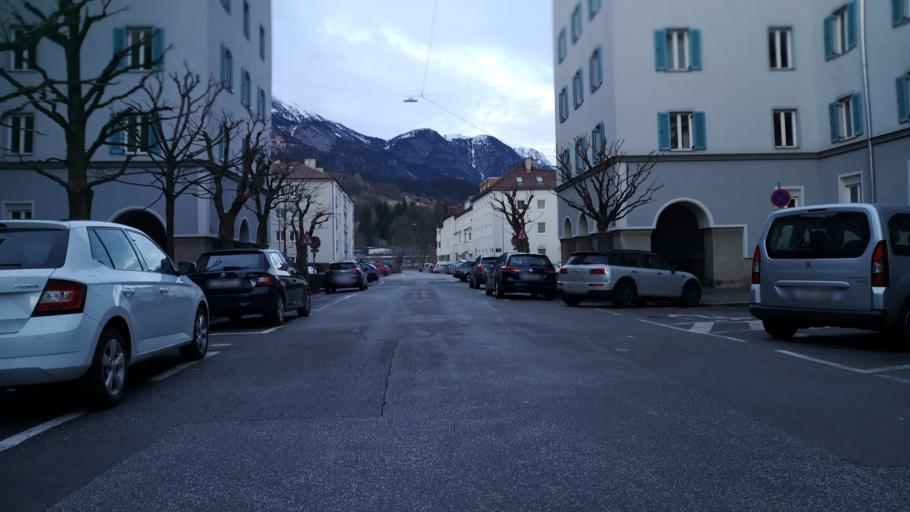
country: AT
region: Tyrol
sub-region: Innsbruck Stadt
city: Innsbruck
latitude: 47.2770
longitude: 11.4092
